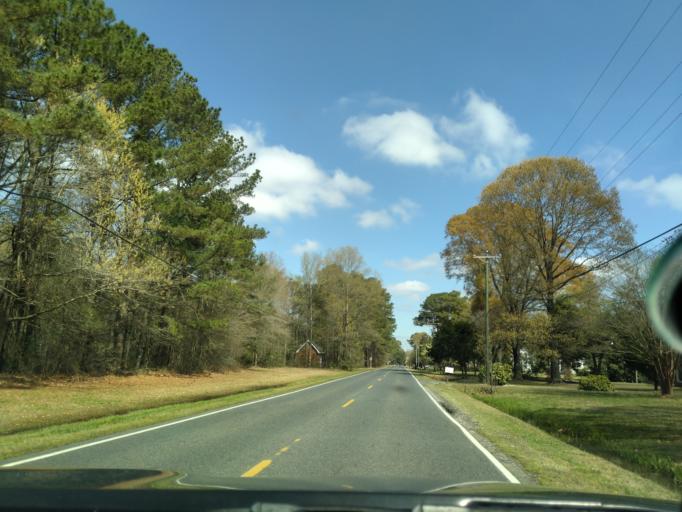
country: US
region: Virginia
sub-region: City of Portsmouth
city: Portsmouth Heights
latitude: 36.7335
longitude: -76.3465
